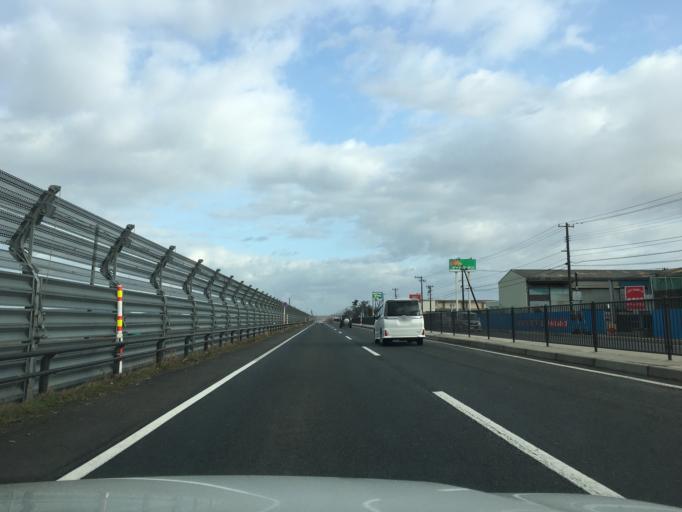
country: JP
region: Yamagata
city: Sakata
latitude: 38.8543
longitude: 139.8467
